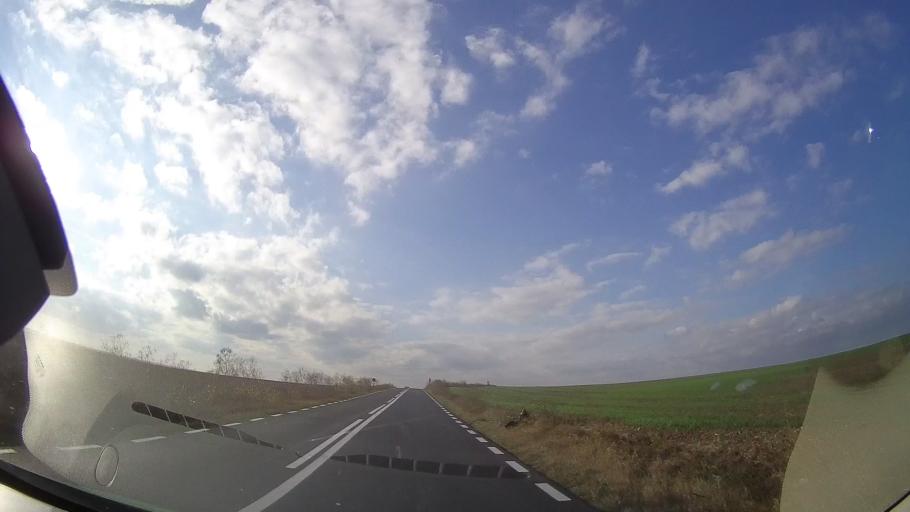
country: RO
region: Constanta
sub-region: Comuna Limanu
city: Limanu
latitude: 43.8239
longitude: 28.5155
